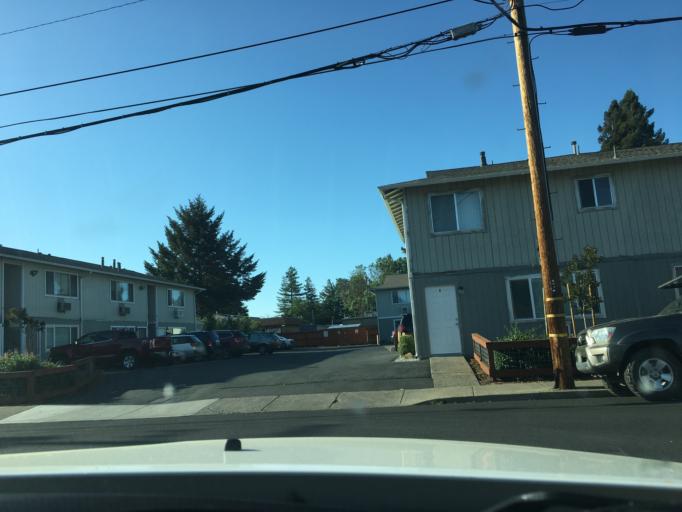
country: US
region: California
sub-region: Mendocino County
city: Ukiah
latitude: 39.1541
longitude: -123.2073
